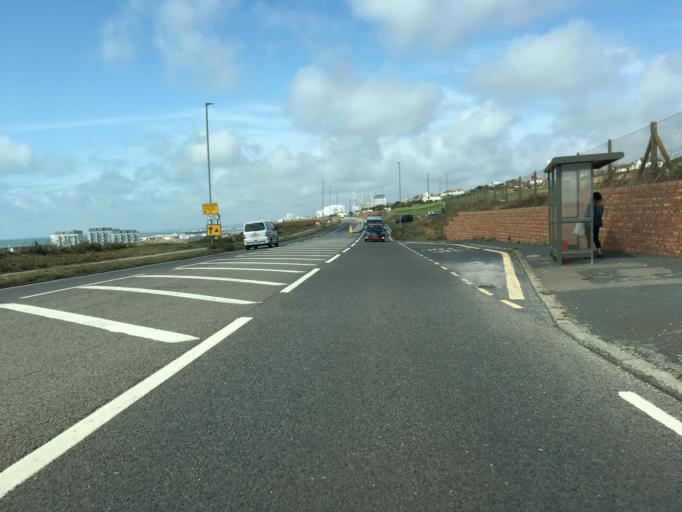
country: GB
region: England
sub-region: Brighton and Hove
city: Rottingdean
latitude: 50.8115
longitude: -0.0880
